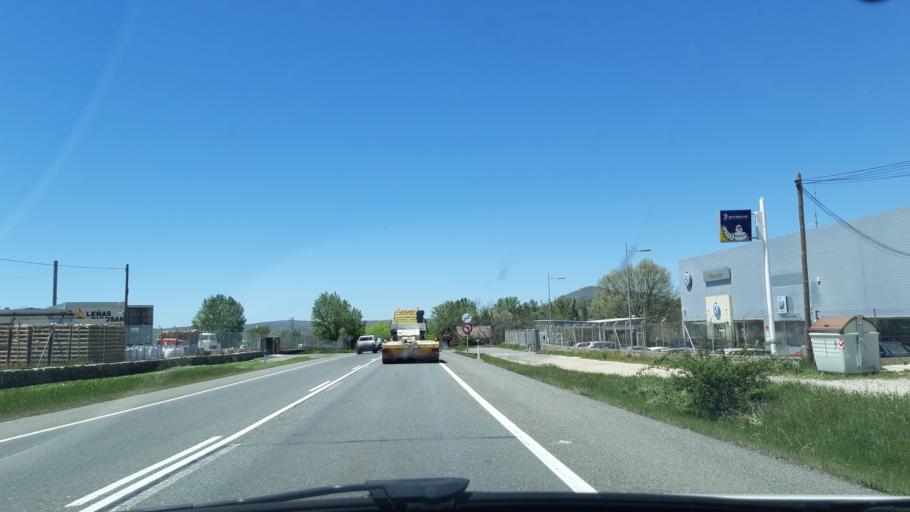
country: ES
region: Castille and Leon
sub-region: Provincia de Avila
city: Peguerinos
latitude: 40.7185
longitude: -4.2097
